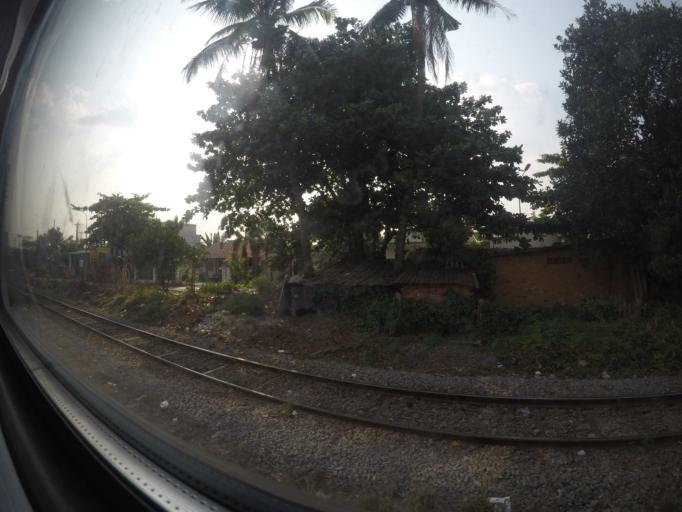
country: VN
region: Binh Duong
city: Di An
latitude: 10.9088
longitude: 106.7701
